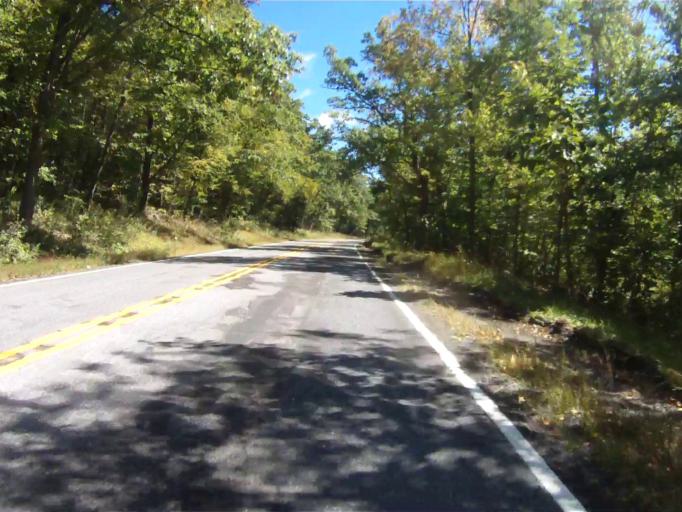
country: US
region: Pennsylvania
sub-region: Centre County
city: Park Forest Village
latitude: 40.9237
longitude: -77.9559
